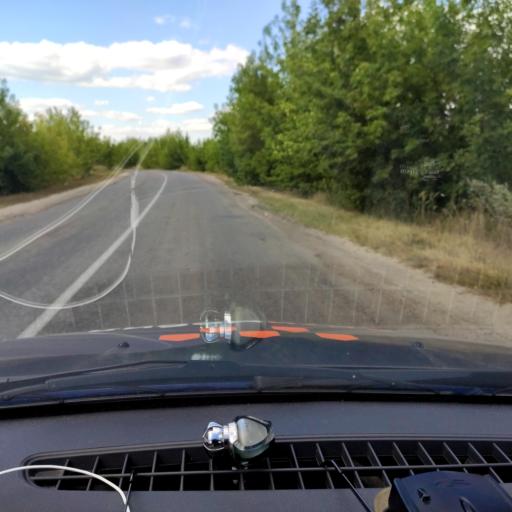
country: RU
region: Voronezj
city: Somovo
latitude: 51.7030
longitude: 39.3733
